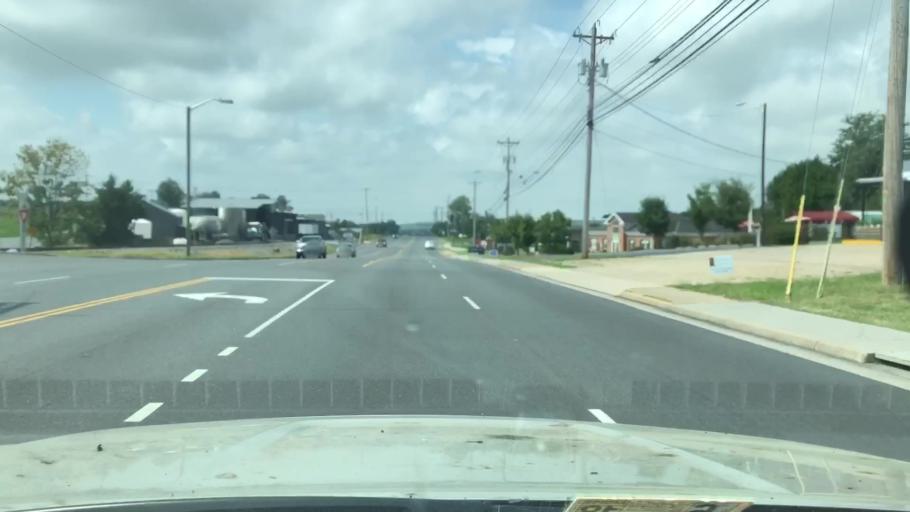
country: US
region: Virginia
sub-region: City of Harrisonburg
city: Harrisonburg
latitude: 38.4336
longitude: -78.8978
